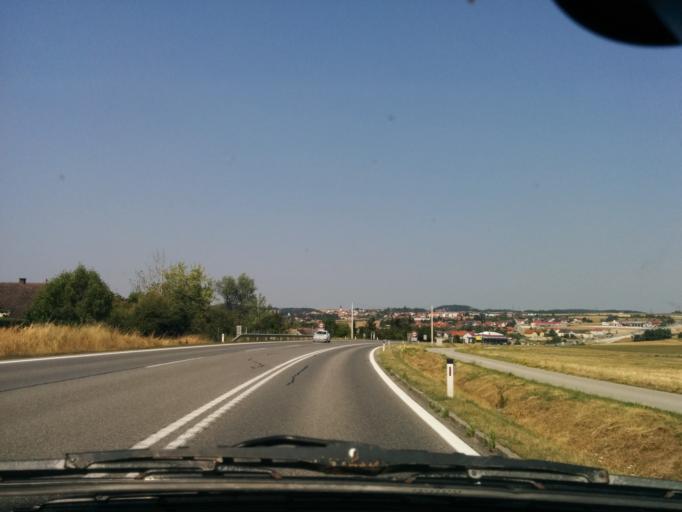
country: AT
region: Lower Austria
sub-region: Politischer Bezirk Krems
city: Gfohl
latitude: 48.5056
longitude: 15.5176
